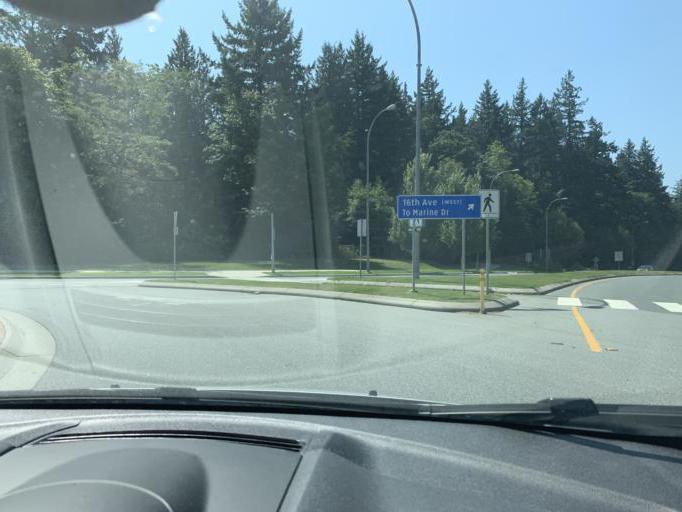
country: CA
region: British Columbia
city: West End
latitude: 49.2543
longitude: -123.2411
